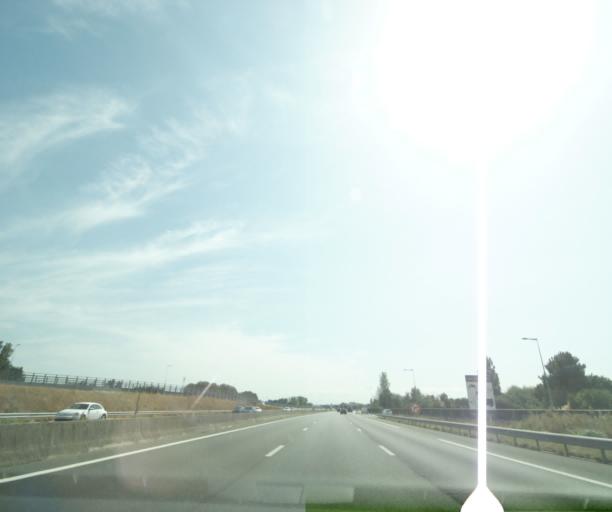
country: FR
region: Aquitaine
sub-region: Departement de la Gironde
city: Cubzac-les-Ponts
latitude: 44.9881
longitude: -0.4274
